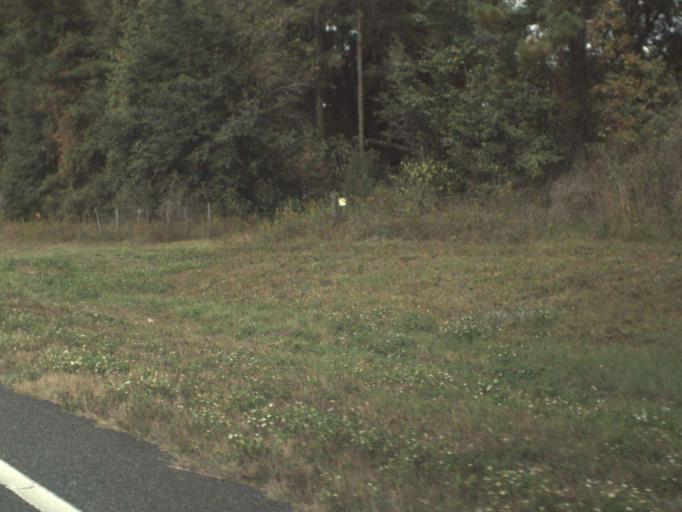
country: US
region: Florida
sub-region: Jefferson County
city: Monticello
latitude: 30.3913
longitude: -83.8649
